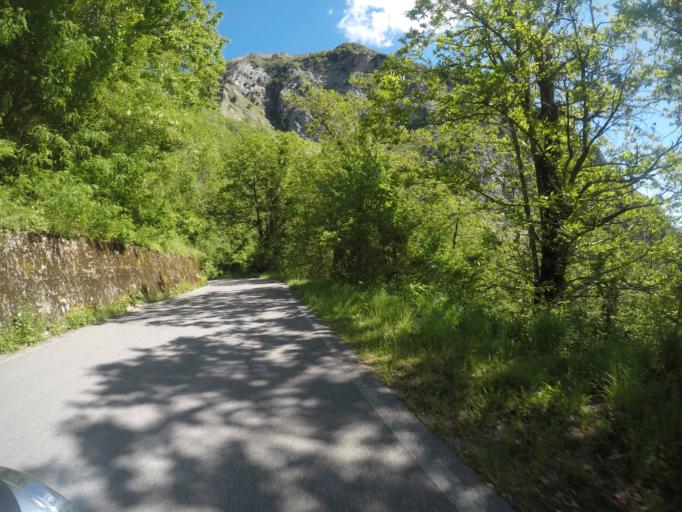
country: IT
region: Tuscany
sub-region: Provincia di Lucca
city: Careggine
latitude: 44.0713
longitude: 10.3187
